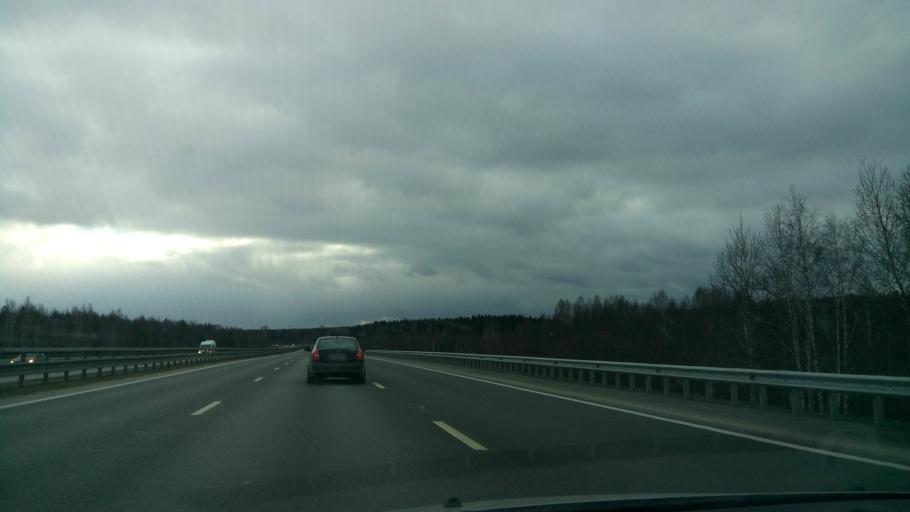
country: RU
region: Sverdlovsk
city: Shuvakish
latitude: 56.9247
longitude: 60.5090
